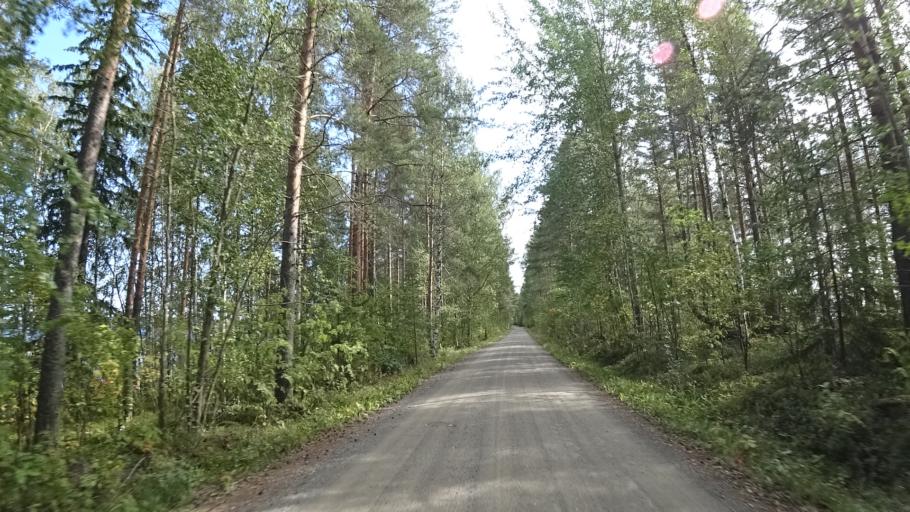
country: FI
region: North Karelia
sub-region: Keski-Karjala
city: Raeaekkylae
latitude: 62.3886
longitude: 29.7866
